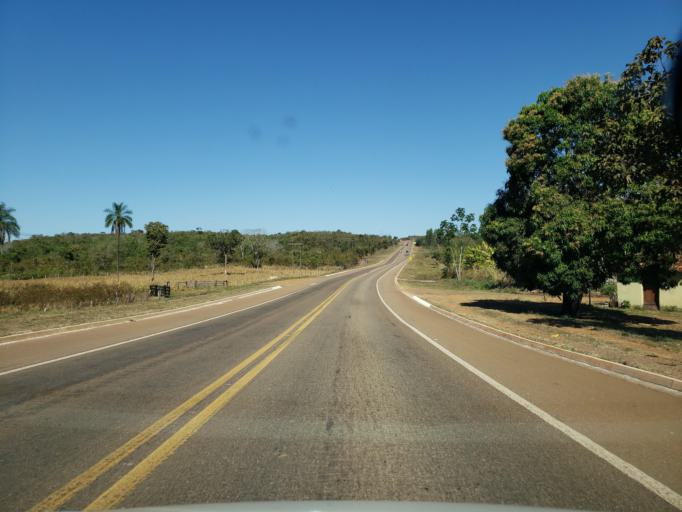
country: BR
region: Mato Grosso
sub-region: Poxoreo
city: Poxoreo
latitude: -15.7817
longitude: -54.3695
